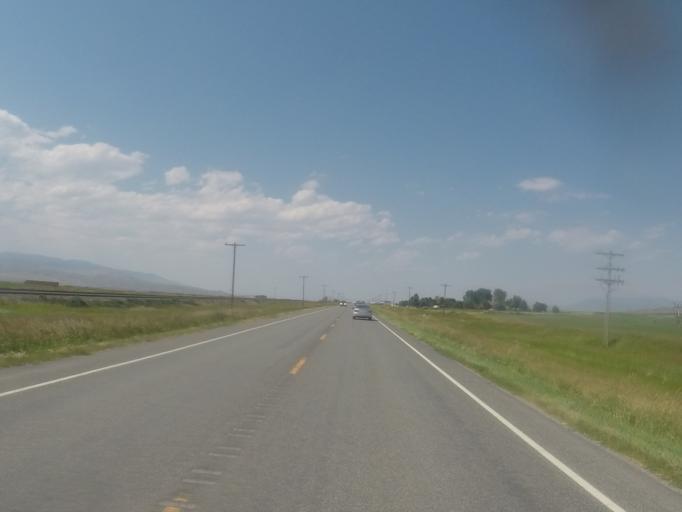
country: US
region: Montana
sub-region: Broadwater County
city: Townsend
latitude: 46.1837
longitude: -111.4459
